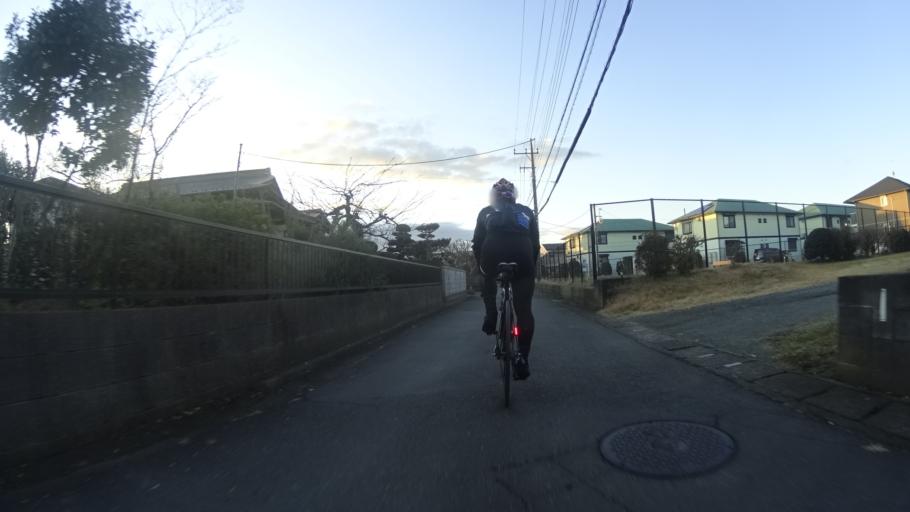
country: JP
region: Kanagawa
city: Zama
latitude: 35.5166
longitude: 139.3682
